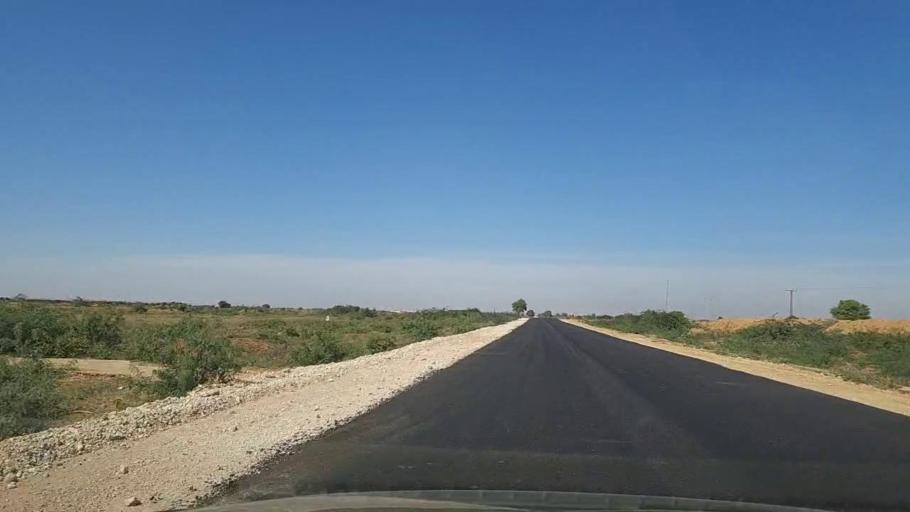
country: PK
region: Sindh
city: Kotri
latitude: 25.2420
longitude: 68.2307
